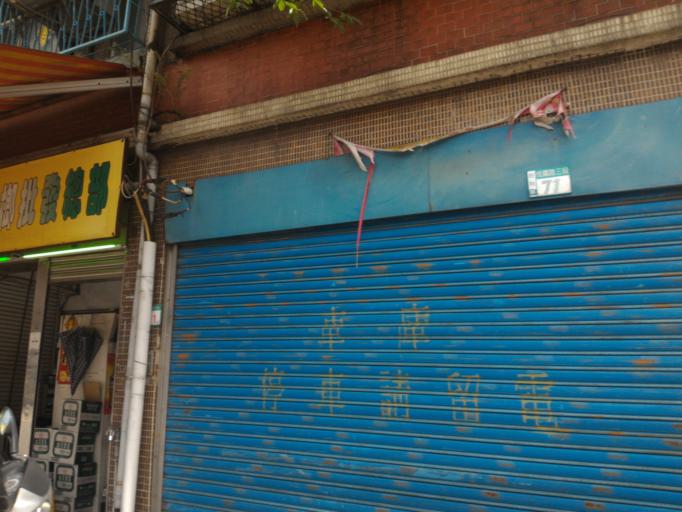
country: TW
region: Taiwan
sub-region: Taoyuan
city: Taoyuan
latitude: 24.9528
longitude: 121.3877
